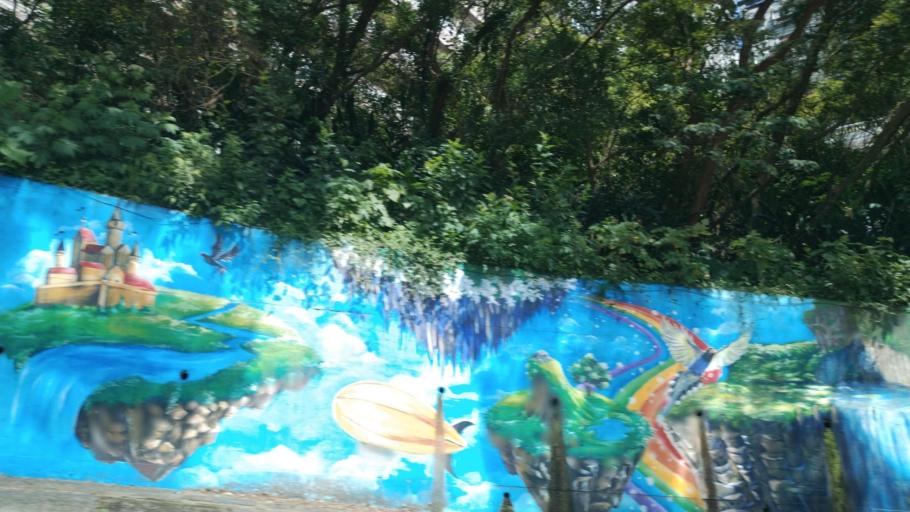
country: TW
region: Taipei
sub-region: Taipei
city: Banqiao
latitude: 24.9413
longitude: 121.5028
